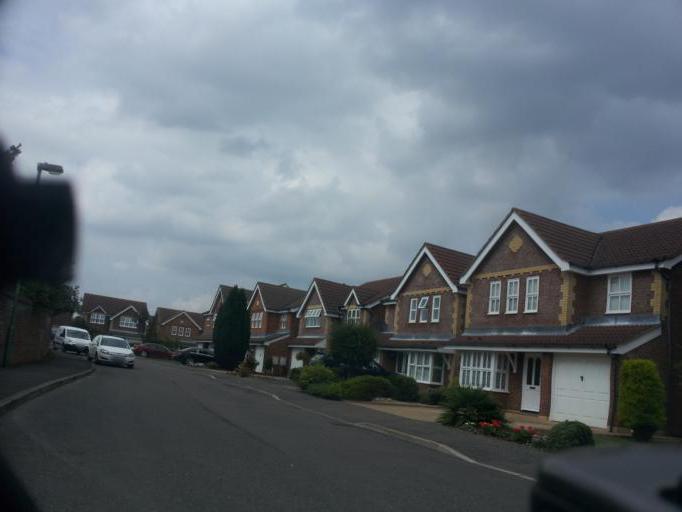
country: GB
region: England
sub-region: Kent
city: Gillingham
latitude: 51.3643
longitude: 0.5675
